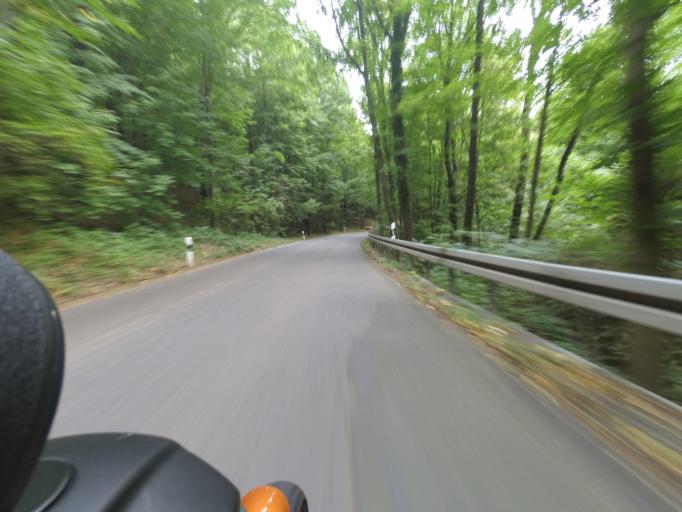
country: DE
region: Saxony
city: Dohna
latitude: 50.9155
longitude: 13.8685
